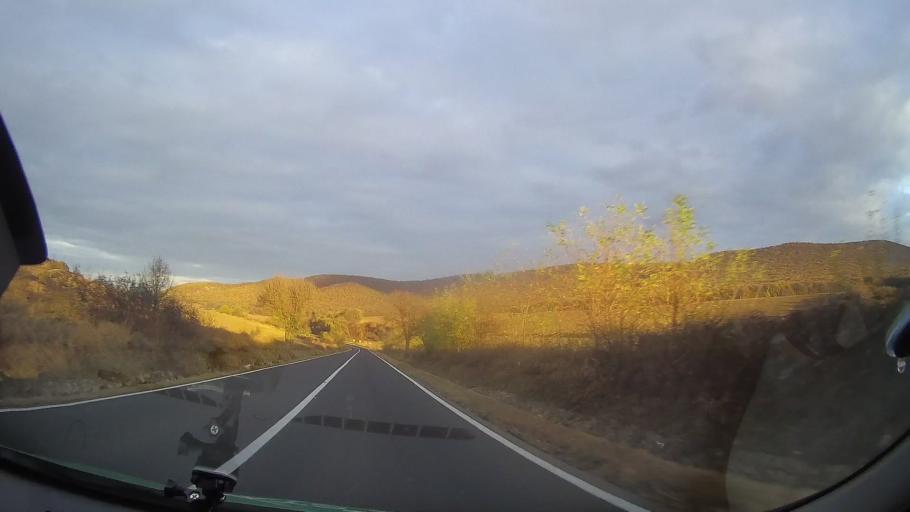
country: RO
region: Tulcea
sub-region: Comuna Ciucurova
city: Ciucurova
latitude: 44.9460
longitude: 28.4981
